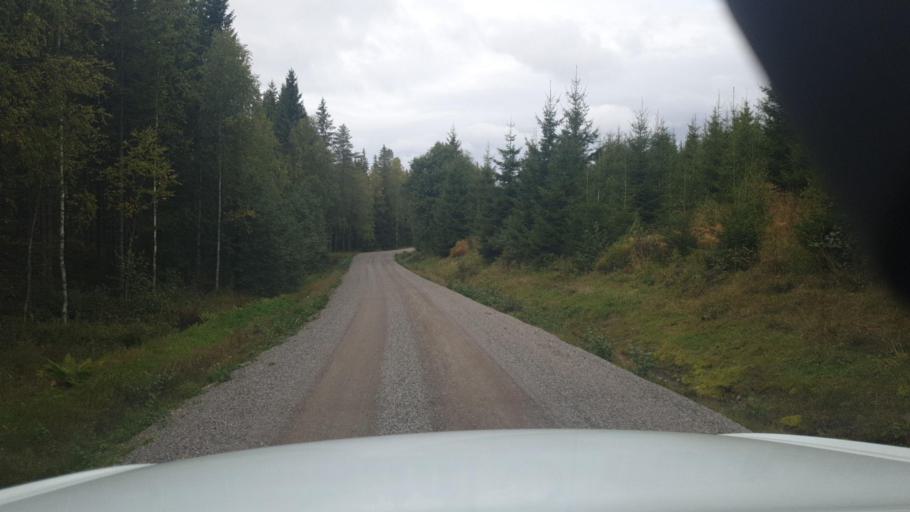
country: SE
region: Vaermland
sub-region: Eda Kommun
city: Charlottenberg
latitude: 60.0545
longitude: 12.6279
